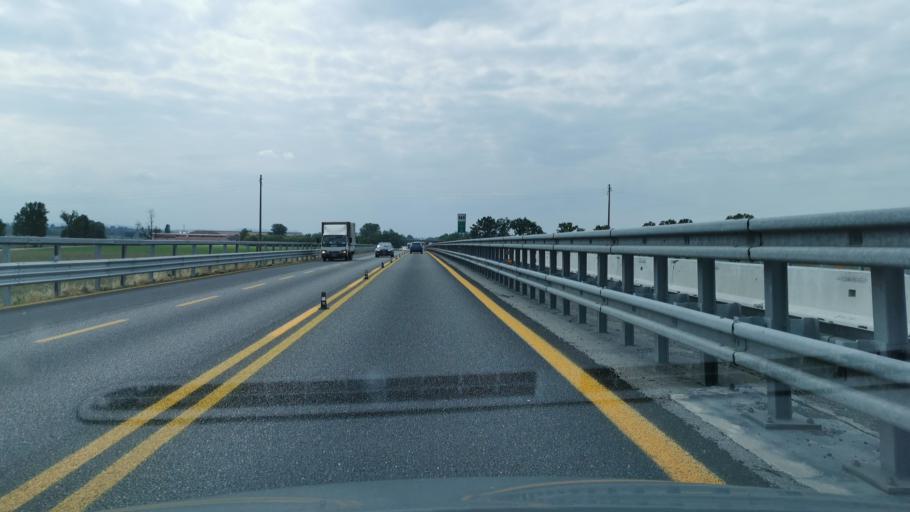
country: IT
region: Emilia-Romagna
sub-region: Provincia di Piacenza
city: Sarmato
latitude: 45.0702
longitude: 9.5021
